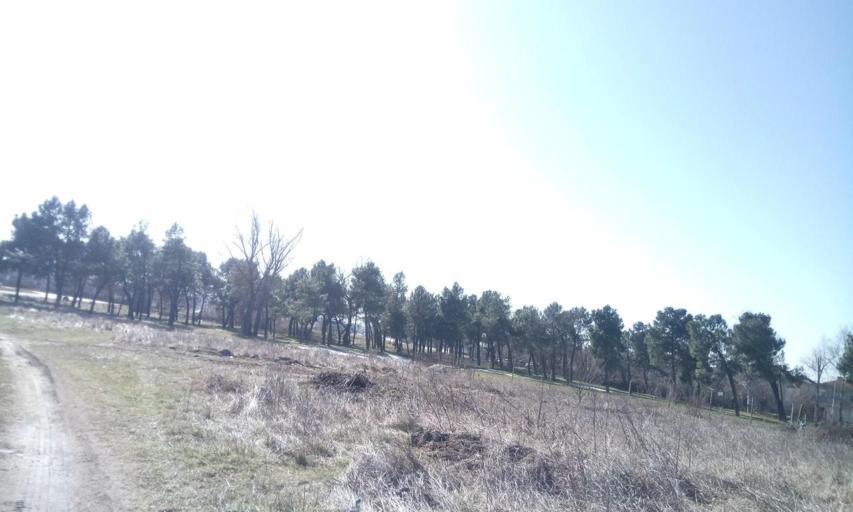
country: BG
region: Plovdiv
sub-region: Obshtina Khisarya
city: Khisarya
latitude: 42.5174
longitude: 24.7211
